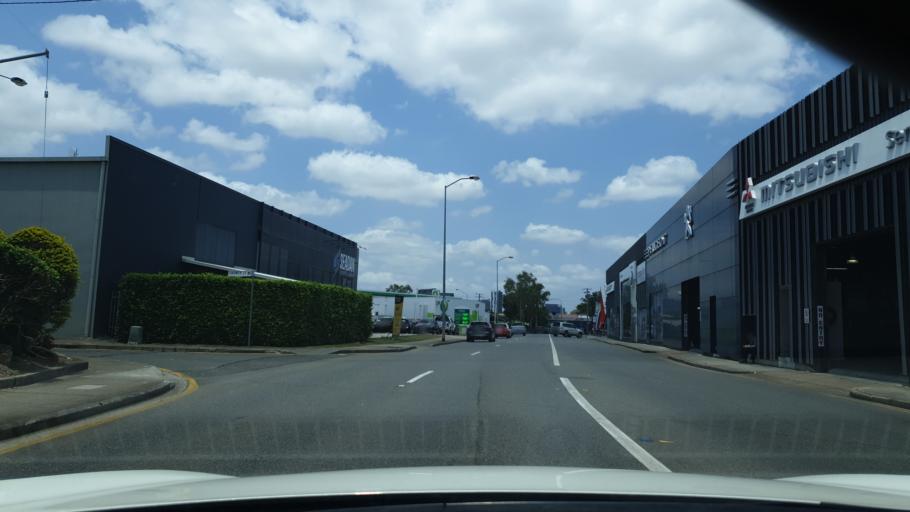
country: AU
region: Queensland
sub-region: Brisbane
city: Wooloowin
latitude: -27.4346
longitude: 153.0410
